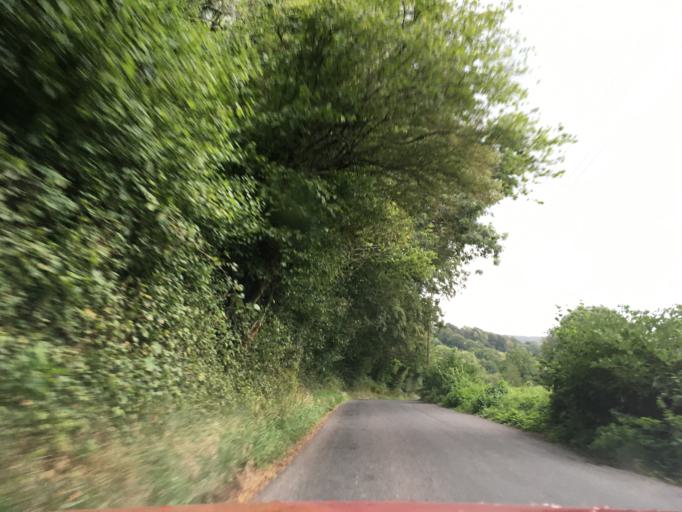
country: GB
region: Wales
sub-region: Monmouthshire
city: Llangybi
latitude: 51.6644
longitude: -2.8860
